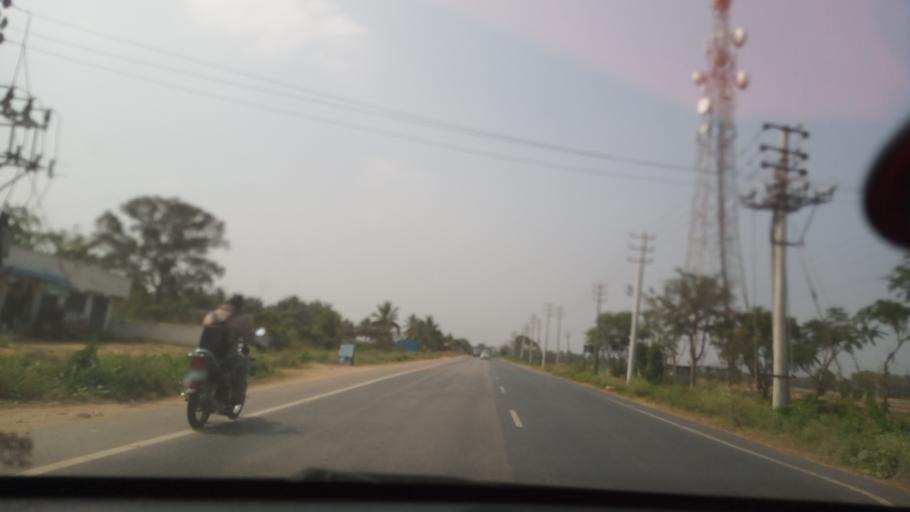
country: IN
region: Karnataka
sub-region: Chamrajnagar
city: Chamrajnagar
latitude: 11.9905
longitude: 76.8663
